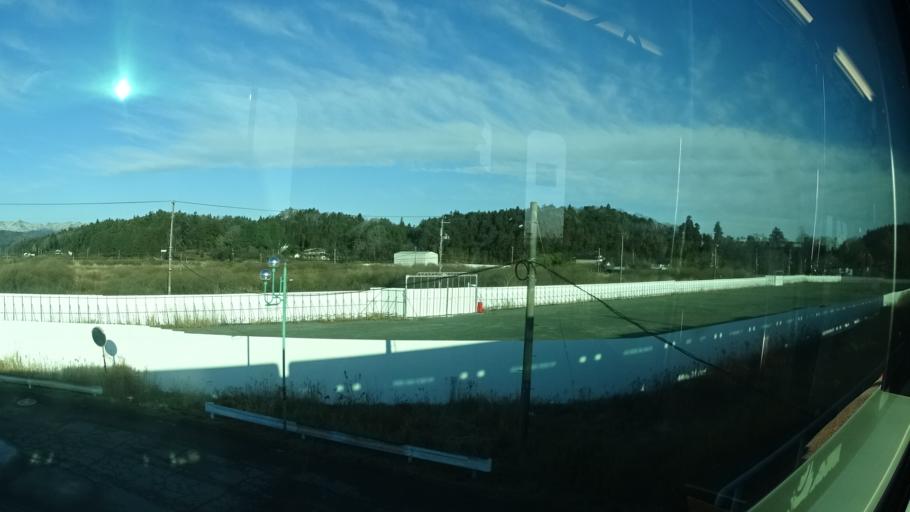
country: JP
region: Fukushima
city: Namie
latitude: 37.4446
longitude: 141.0028
